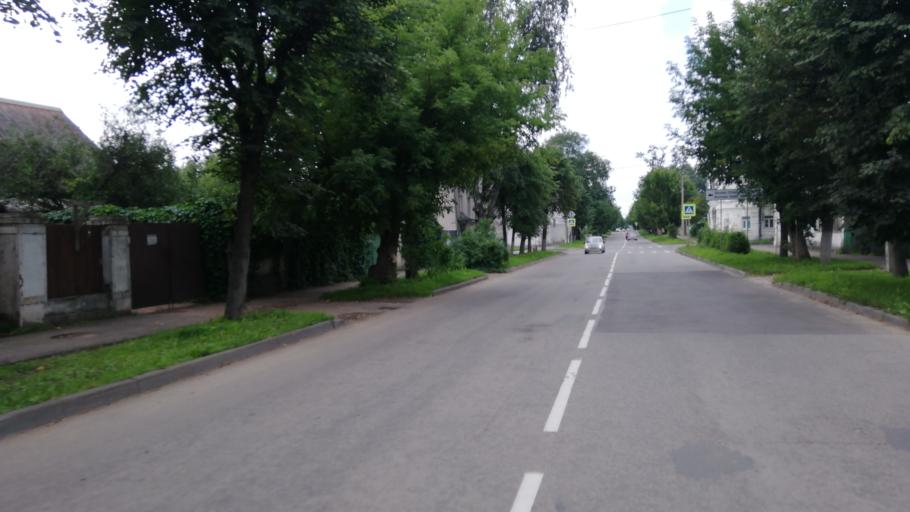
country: RU
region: Kostroma
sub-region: Kostromskoy Rayon
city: Kostroma
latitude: 57.7709
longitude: 40.9159
